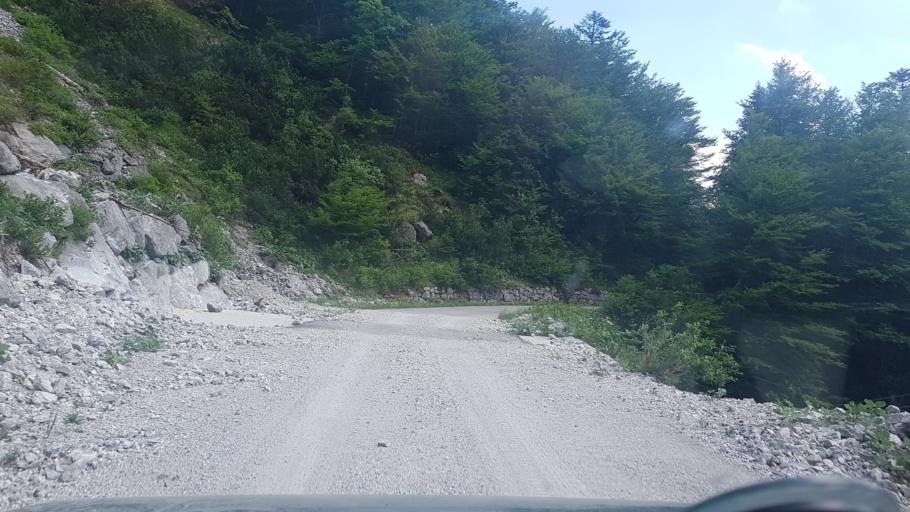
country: IT
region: Friuli Venezia Giulia
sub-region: Provincia di Udine
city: Paularo
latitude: 46.5500
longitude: 13.2023
